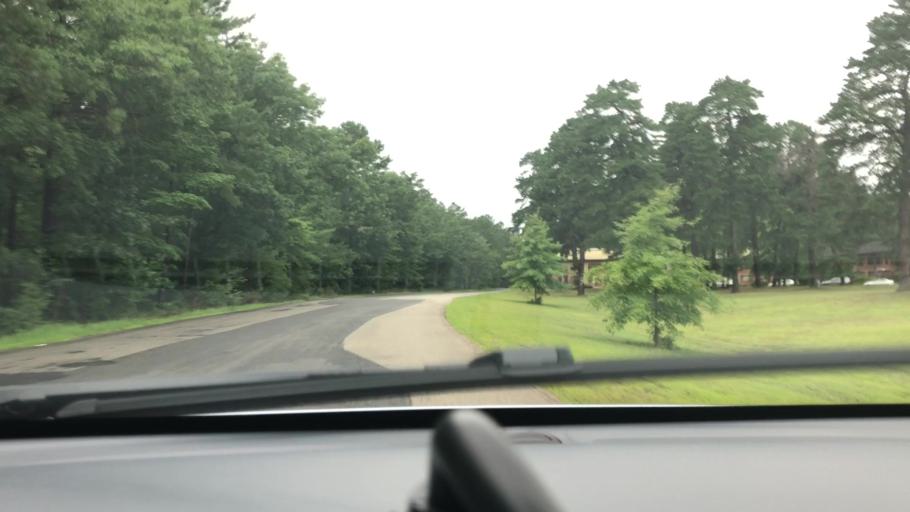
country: US
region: New Hampshire
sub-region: Hillsborough County
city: Pinardville
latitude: 42.9983
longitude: -71.4942
